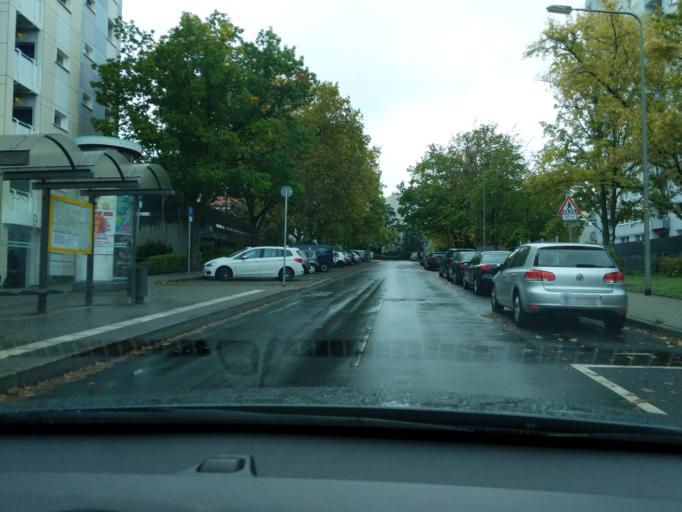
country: DE
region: Hesse
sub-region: Regierungsbezirk Darmstadt
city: Bad Vilbel
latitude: 50.1406
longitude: 8.7195
